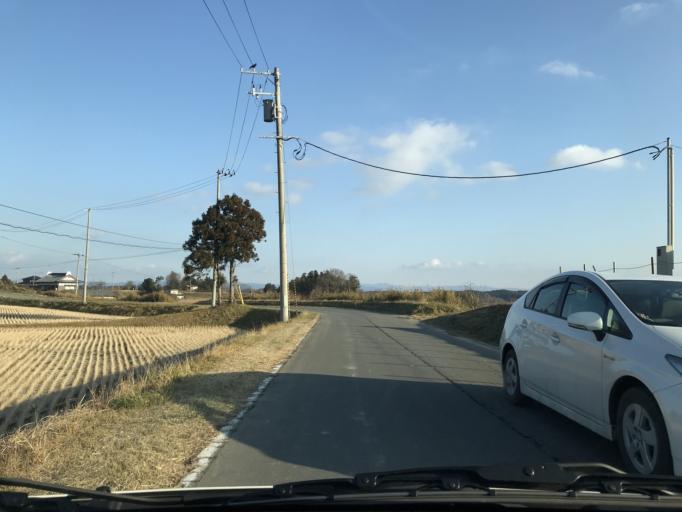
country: JP
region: Miyagi
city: Wakuya
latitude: 38.6944
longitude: 141.1111
